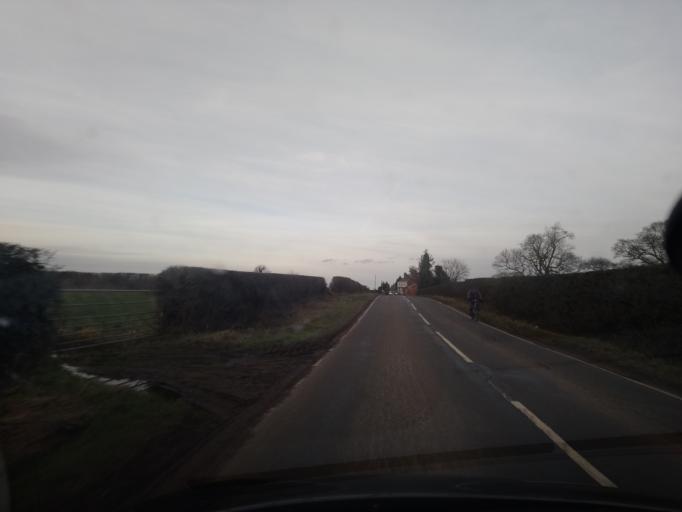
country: GB
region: England
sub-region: Shropshire
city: Prees
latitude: 52.9129
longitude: -2.6837
